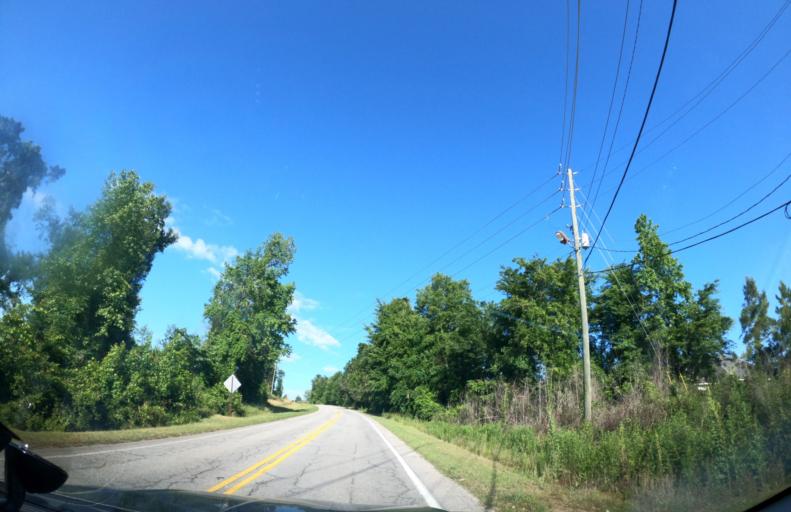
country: US
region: Georgia
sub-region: Columbia County
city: Grovetown
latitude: 33.4566
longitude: -82.2346
